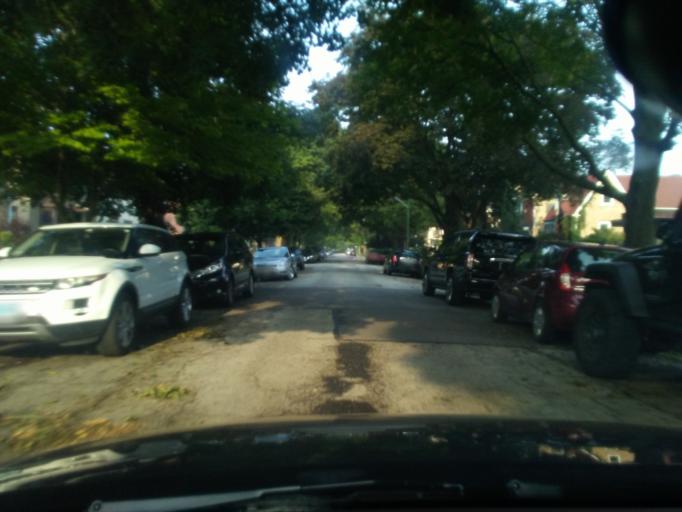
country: US
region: Illinois
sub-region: Cook County
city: Lincolnwood
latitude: 42.0129
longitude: -87.7051
